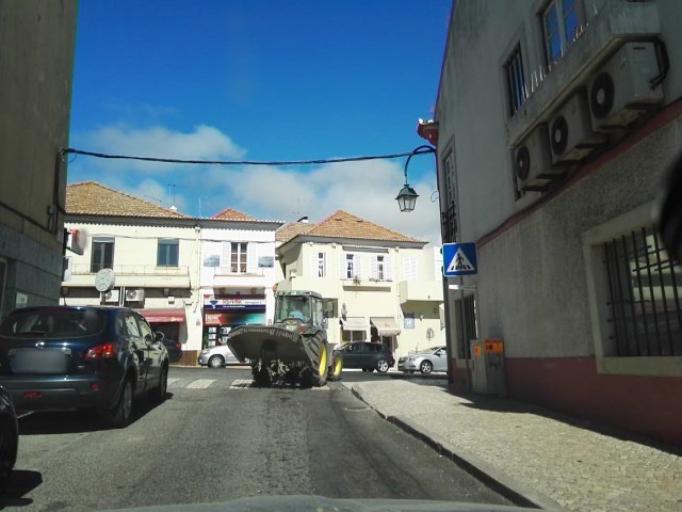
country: PT
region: Lisbon
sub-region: Arruda Dos Vinhos
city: Arruda dos Vinhos
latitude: 38.9828
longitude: -9.0774
